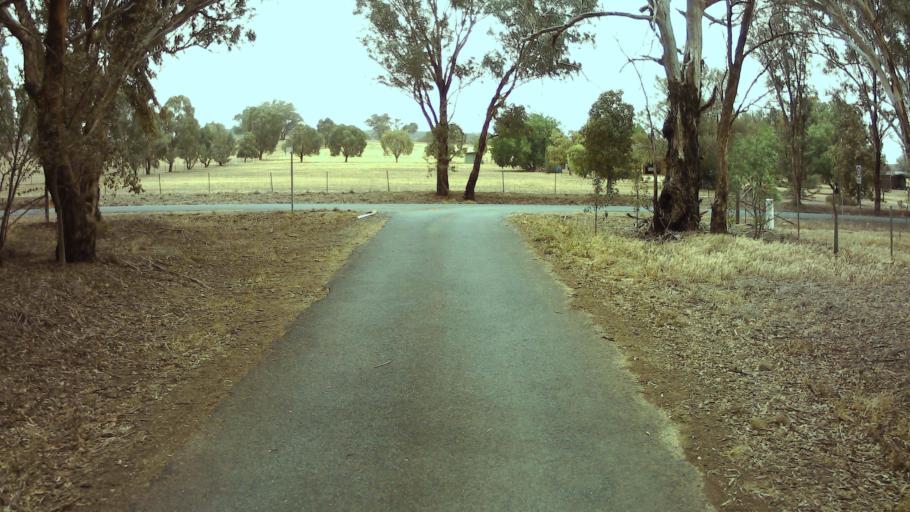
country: AU
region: New South Wales
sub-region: Weddin
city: Grenfell
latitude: -33.8959
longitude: 148.1433
